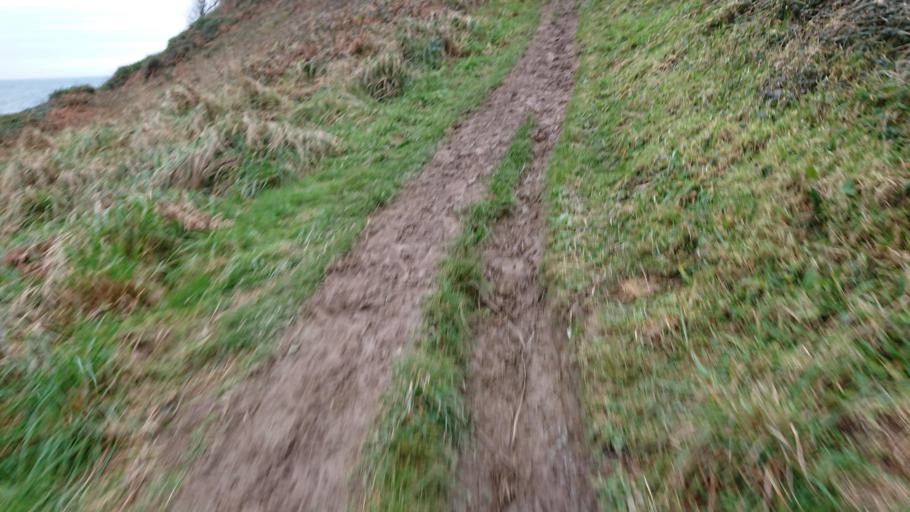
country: GB
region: England
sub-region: Cornwall
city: Fowey
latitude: 50.3331
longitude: -4.5783
